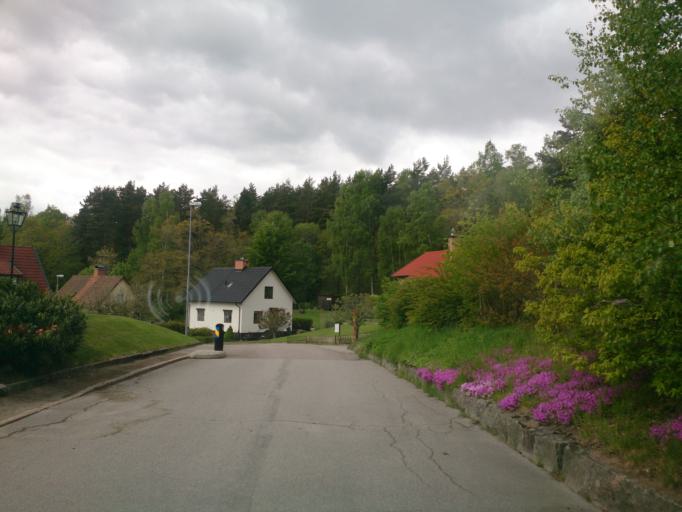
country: SE
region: OEstergoetland
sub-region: Atvidabergs Kommun
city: Atvidaberg
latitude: 58.2073
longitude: 16.0035
